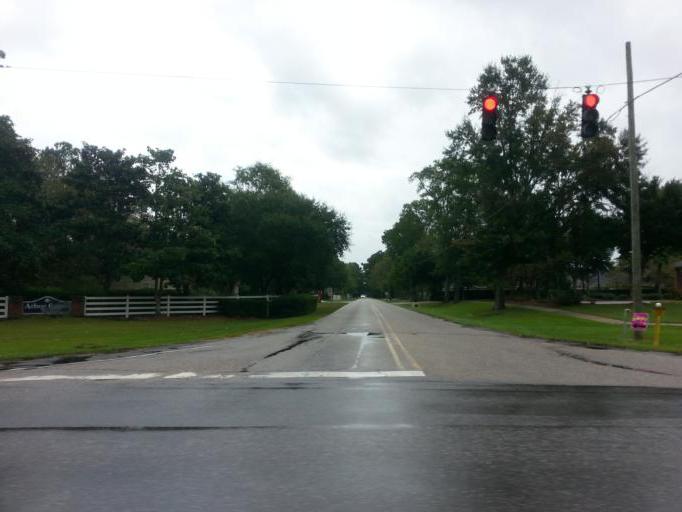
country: US
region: Alabama
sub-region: Baldwin County
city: Fairhope
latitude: 30.5310
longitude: -87.8861
